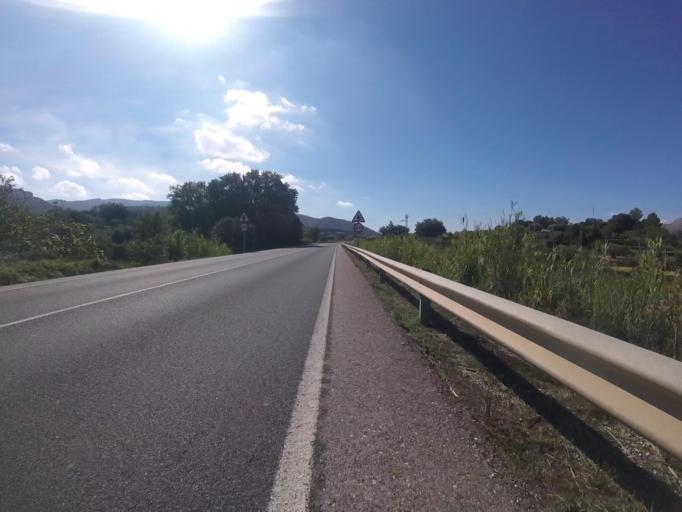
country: ES
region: Valencia
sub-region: Provincia de Castello
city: Sarratella
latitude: 40.3299
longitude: -0.0157
